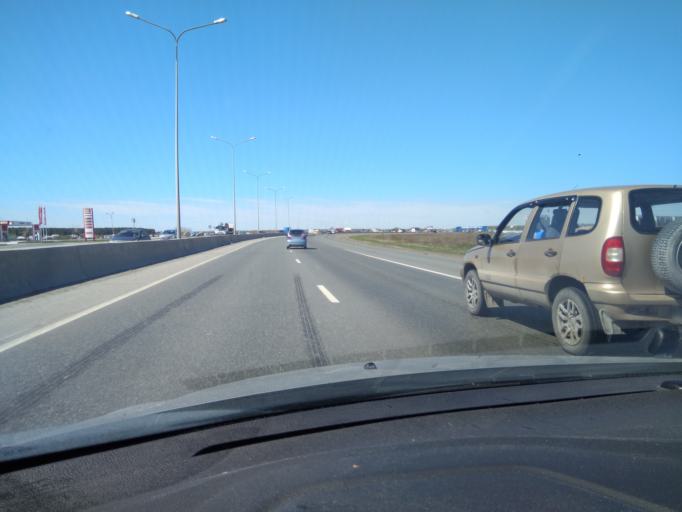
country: RU
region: Tjumen
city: Moskovskiy
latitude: 57.1351
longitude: 65.4626
